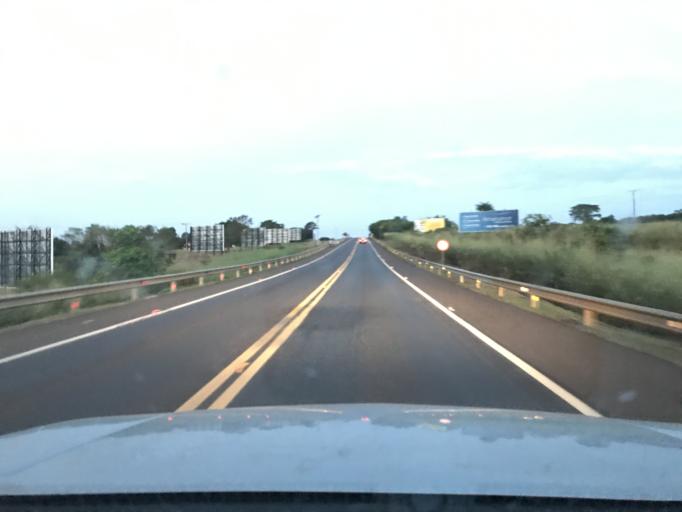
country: PY
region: Canindeyu
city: Salto del Guaira
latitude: -24.0095
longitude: -54.3066
